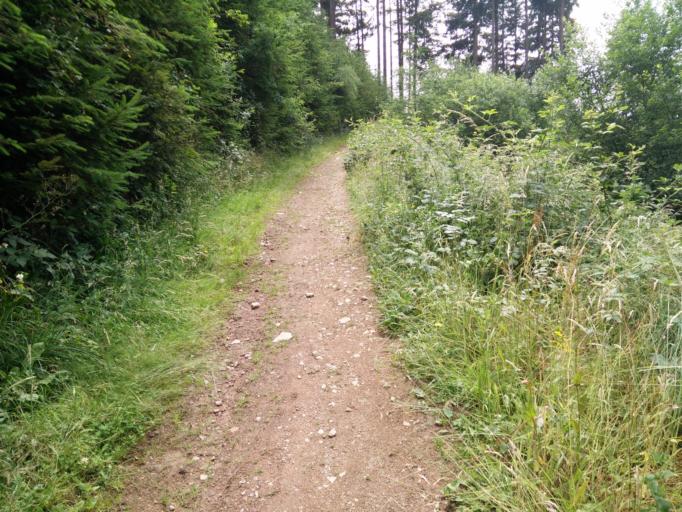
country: FR
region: Rhone-Alpes
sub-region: Departement du Rhone
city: Cublize
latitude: 46.0055
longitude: 4.3726
